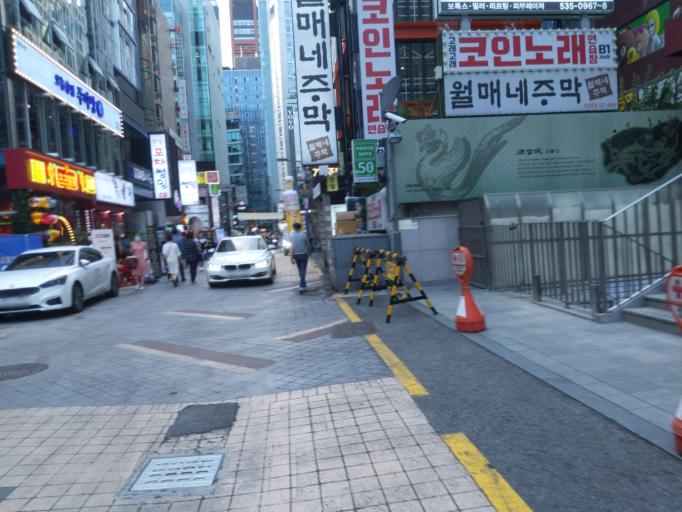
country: KR
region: Seoul
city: Seoul
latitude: 37.5010
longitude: 127.0255
